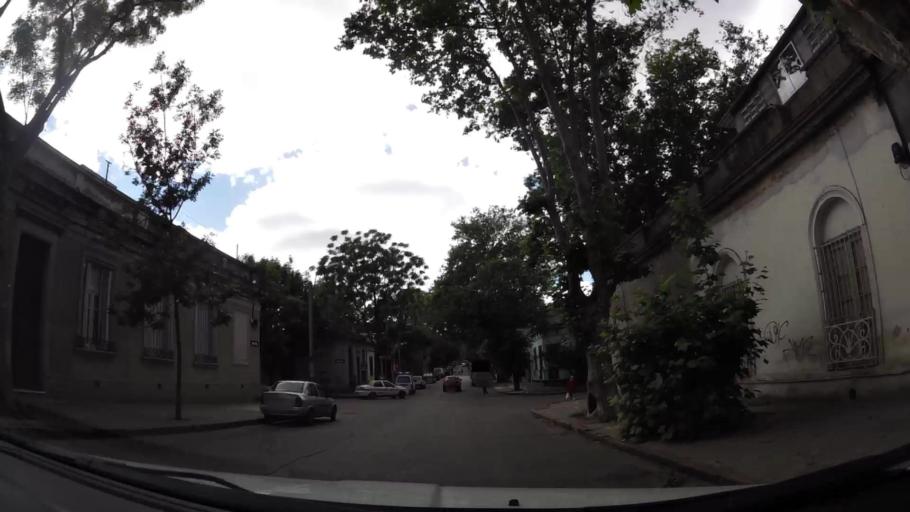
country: UY
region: Montevideo
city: Montevideo
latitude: -34.8772
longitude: -56.1835
